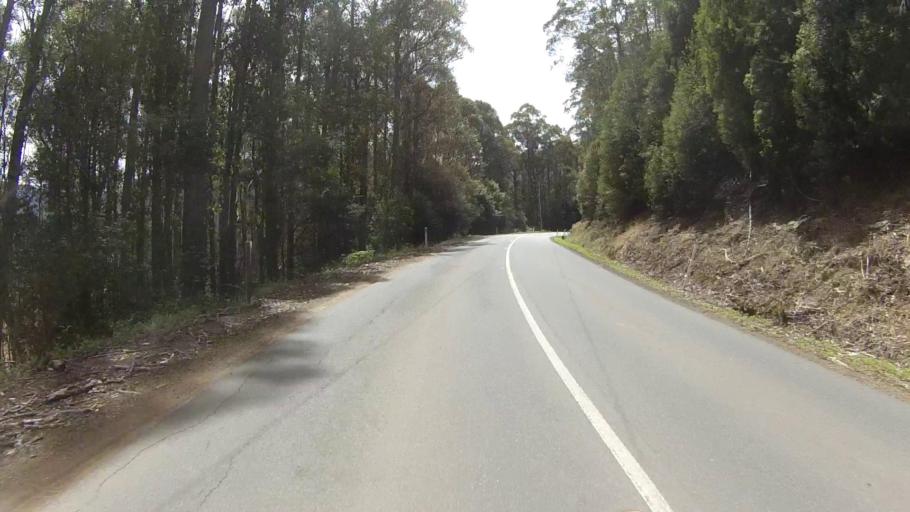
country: AU
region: Tasmania
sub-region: Kingborough
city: Kettering
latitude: -43.1275
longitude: 147.1677
